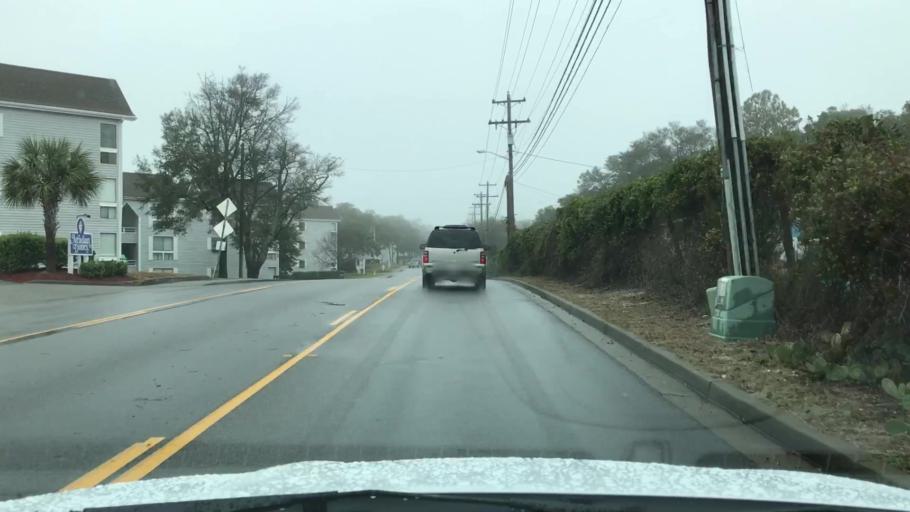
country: US
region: South Carolina
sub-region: Horry County
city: North Myrtle Beach
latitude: 33.7646
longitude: -78.7859
